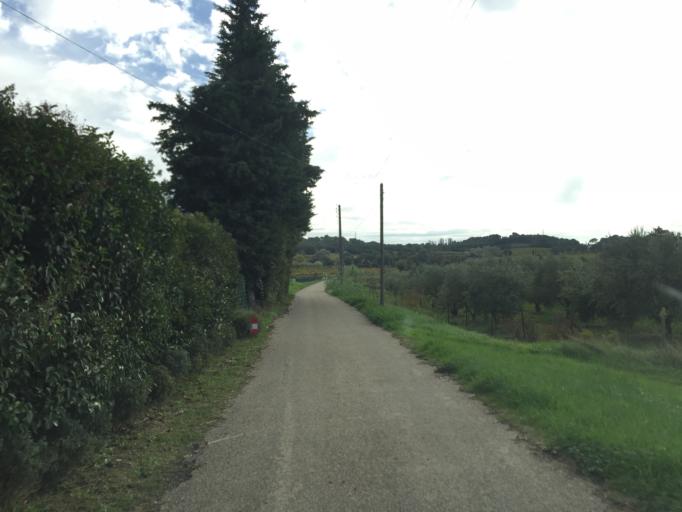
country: FR
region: Provence-Alpes-Cote d'Azur
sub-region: Departement du Vaucluse
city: Orange
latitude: 44.0974
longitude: 4.8120
